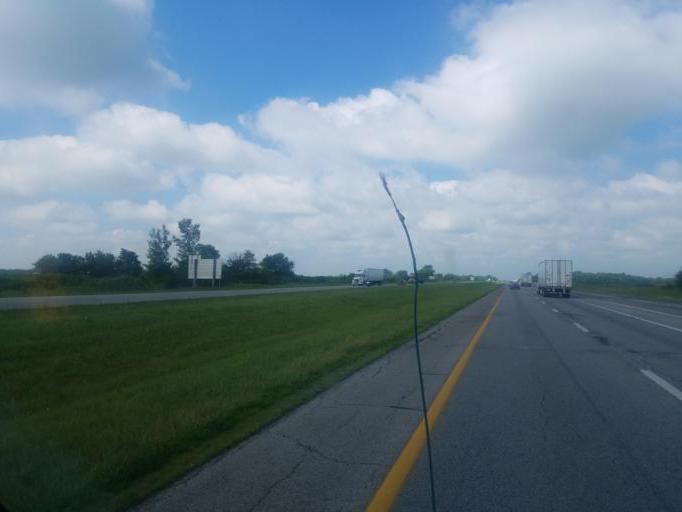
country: US
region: Ohio
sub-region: Madison County
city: Mount Sterling
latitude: 39.7560
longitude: -83.3078
